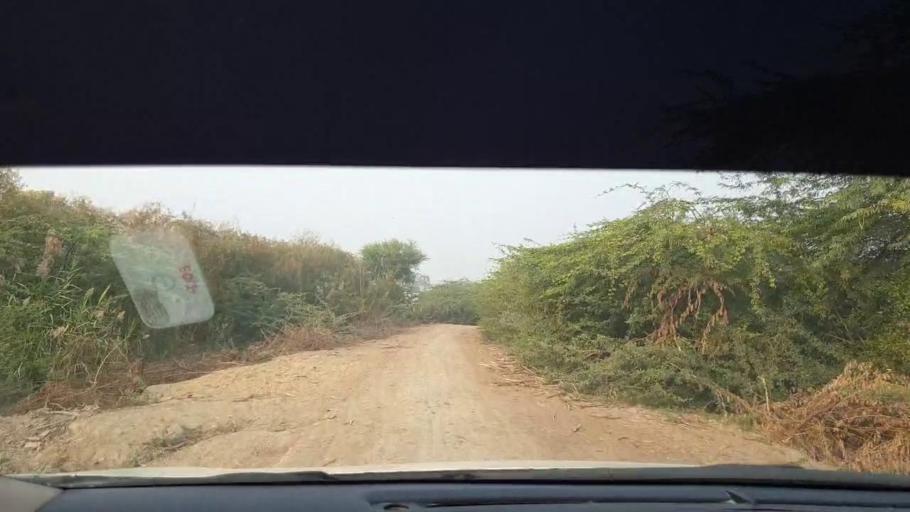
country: PK
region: Sindh
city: Berani
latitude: 25.8016
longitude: 68.8523
